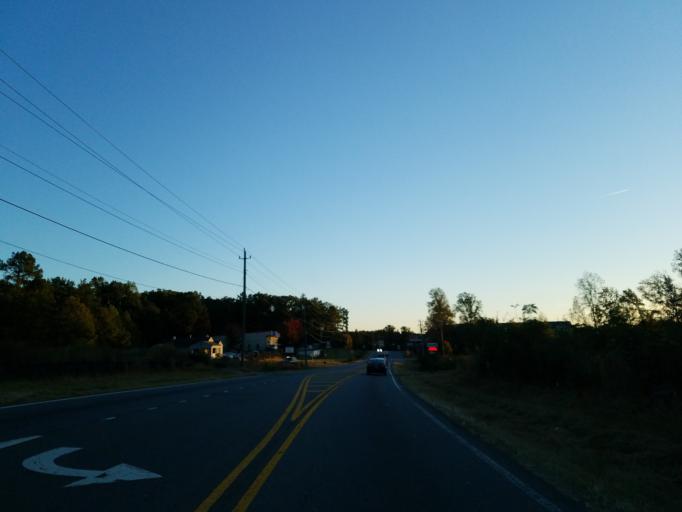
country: US
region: Georgia
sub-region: Forsyth County
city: Cumming
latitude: 34.1845
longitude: -84.1459
